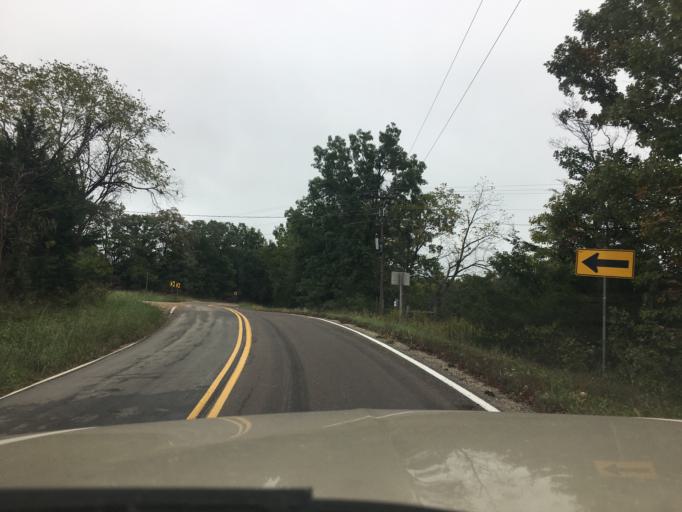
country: US
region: Missouri
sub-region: Crawford County
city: Cuba
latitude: 38.1908
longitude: -91.4804
